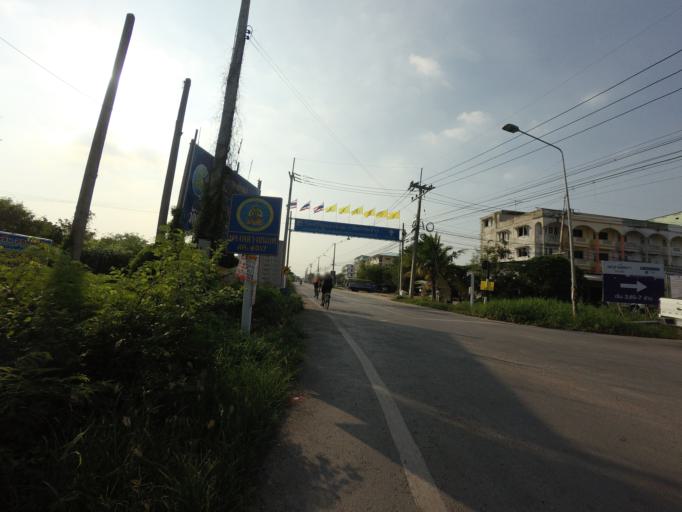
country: TH
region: Samut Sakhon
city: Samut Sakhon
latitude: 13.5139
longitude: 100.2959
